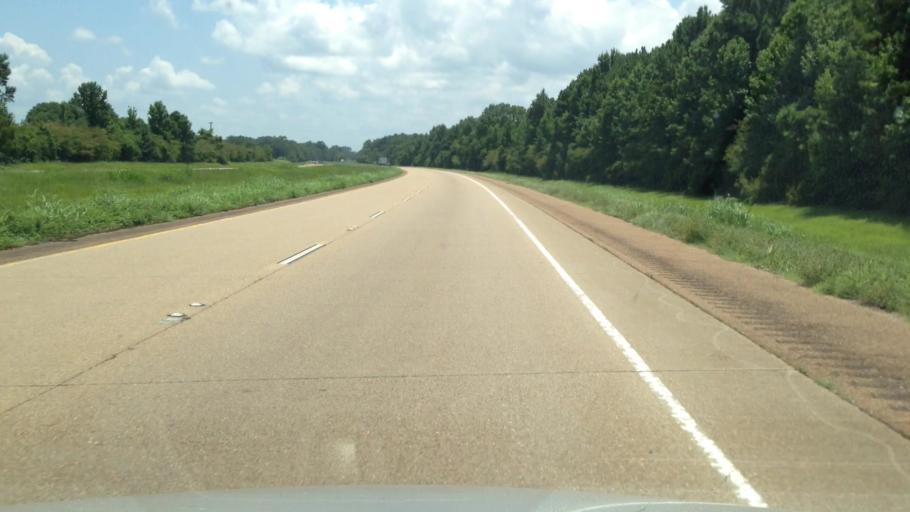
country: US
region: Louisiana
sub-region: Rapides Parish
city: Woodworth
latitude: 31.1408
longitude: -92.4515
